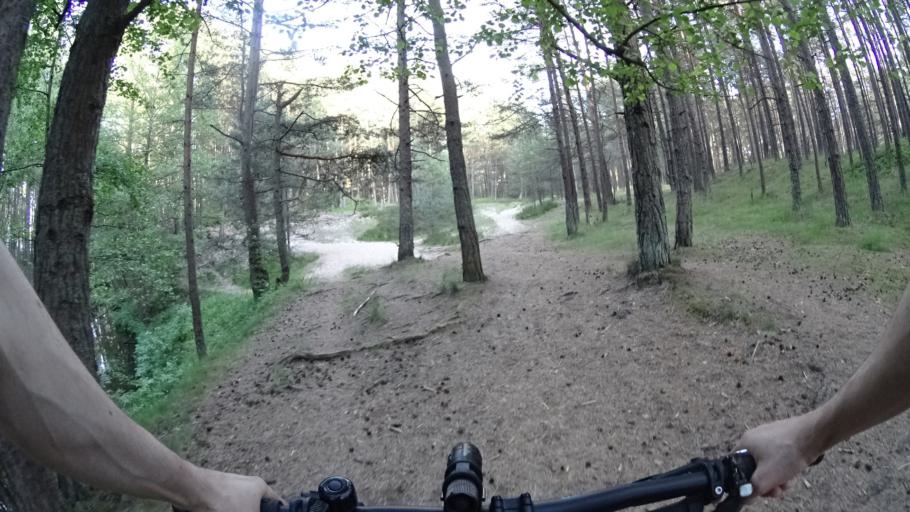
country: LV
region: Riga
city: Jaunciems
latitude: 57.1097
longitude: 24.1879
